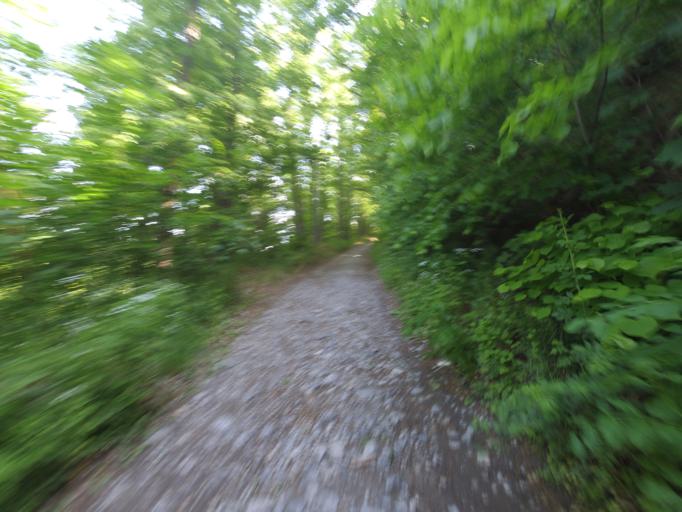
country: DE
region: Thuringia
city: Rudolstadt
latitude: 50.7075
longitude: 11.3297
